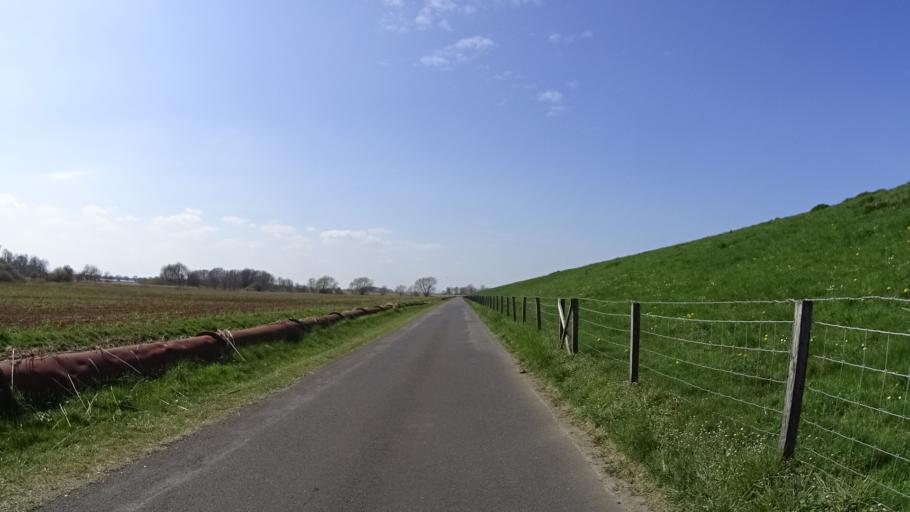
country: DE
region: Lower Saxony
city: Papenburg
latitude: 53.1014
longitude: 7.3495
